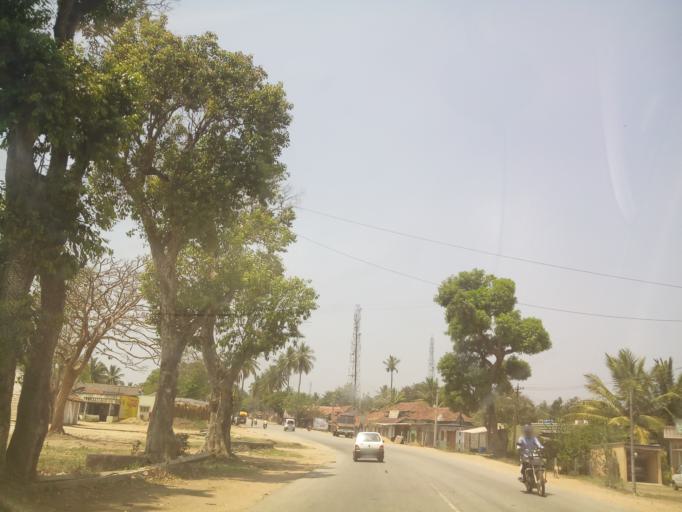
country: IN
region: Karnataka
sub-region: Hassan
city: Alur
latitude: 12.9497
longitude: 75.9422
